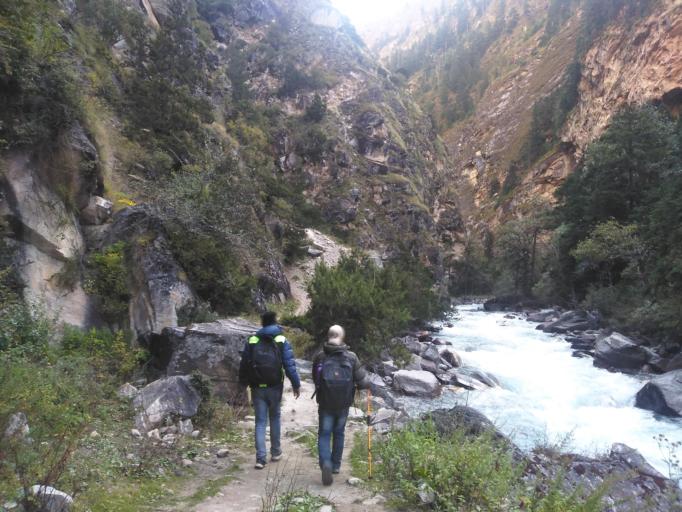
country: NP
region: Western Region
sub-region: Dhawalagiri Zone
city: Jomsom
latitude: 28.9319
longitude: 83.0460
